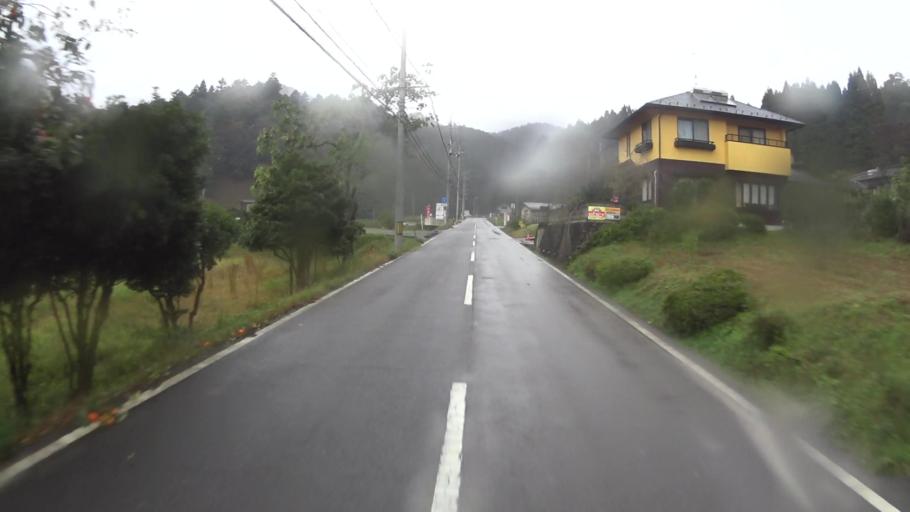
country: JP
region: Kyoto
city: Miyazu
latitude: 35.4266
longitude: 135.1575
